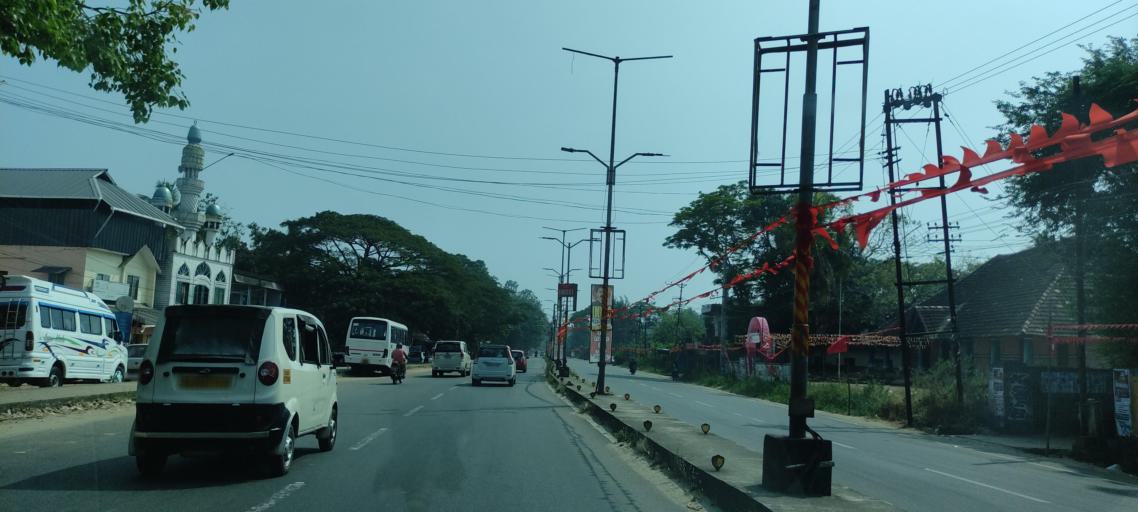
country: IN
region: Kerala
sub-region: Alappuzha
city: Alleppey
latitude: 9.3825
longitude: 76.3557
